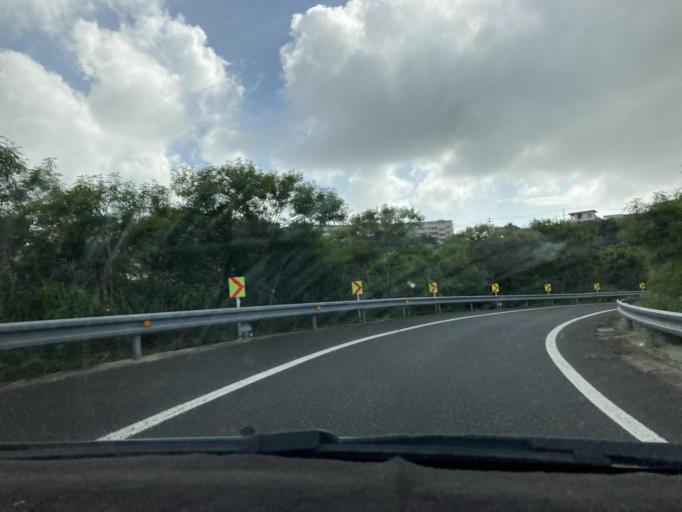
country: JP
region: Okinawa
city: Tomigusuku
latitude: 26.1720
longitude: 127.6976
